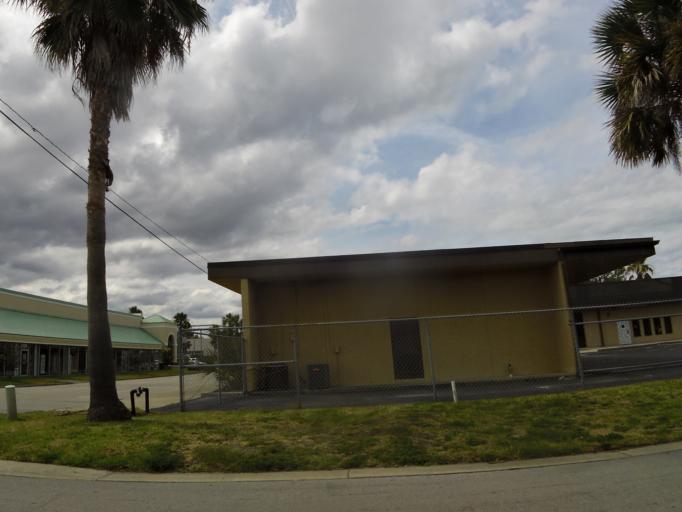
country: US
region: Florida
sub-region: Duval County
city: Jacksonville Beach
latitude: 30.2867
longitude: -81.4011
